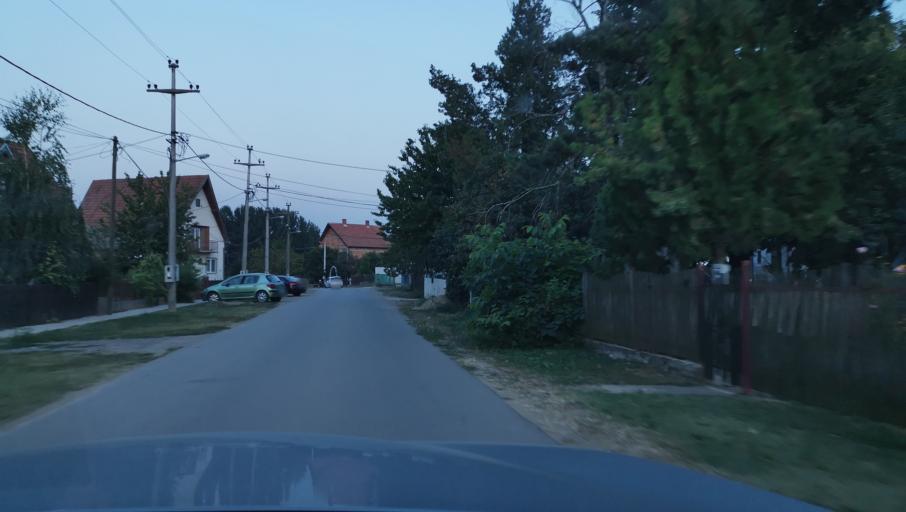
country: RS
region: Central Serbia
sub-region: Belgrade
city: Obrenovac
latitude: 44.6812
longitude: 20.2204
